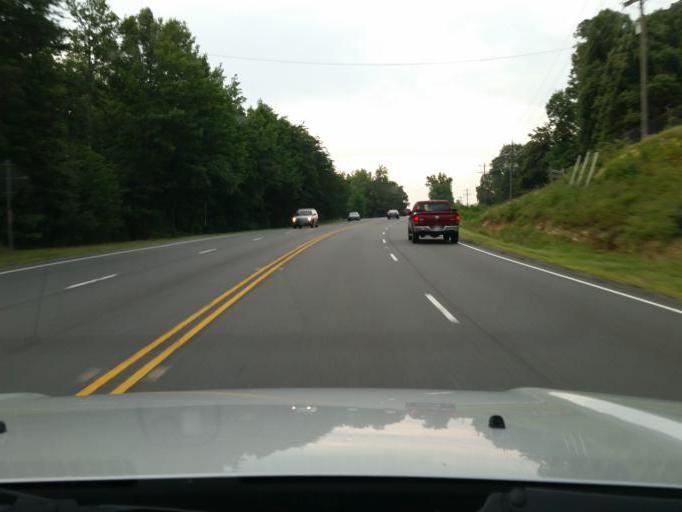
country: US
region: Virginia
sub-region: Spotsylvania County
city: Spotsylvania Courthouse
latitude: 38.2090
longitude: -77.5076
